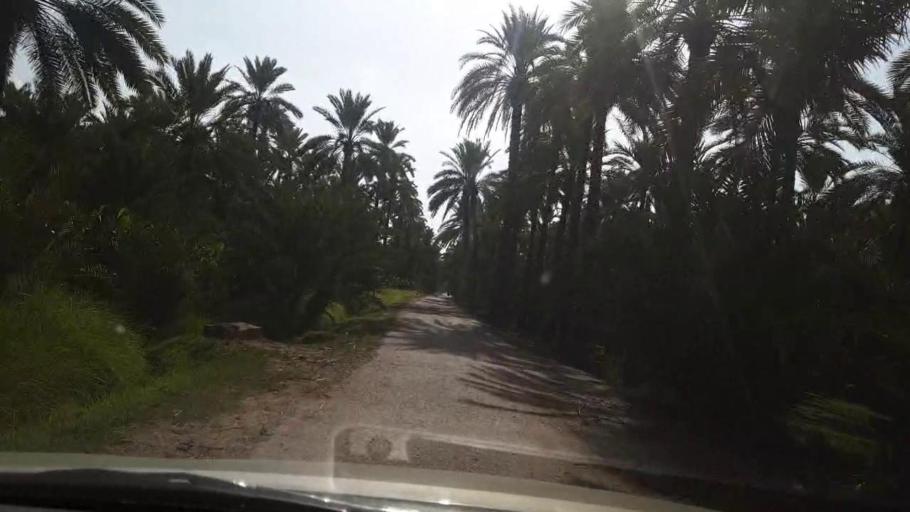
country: PK
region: Sindh
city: Sukkur
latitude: 27.6423
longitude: 68.8168
